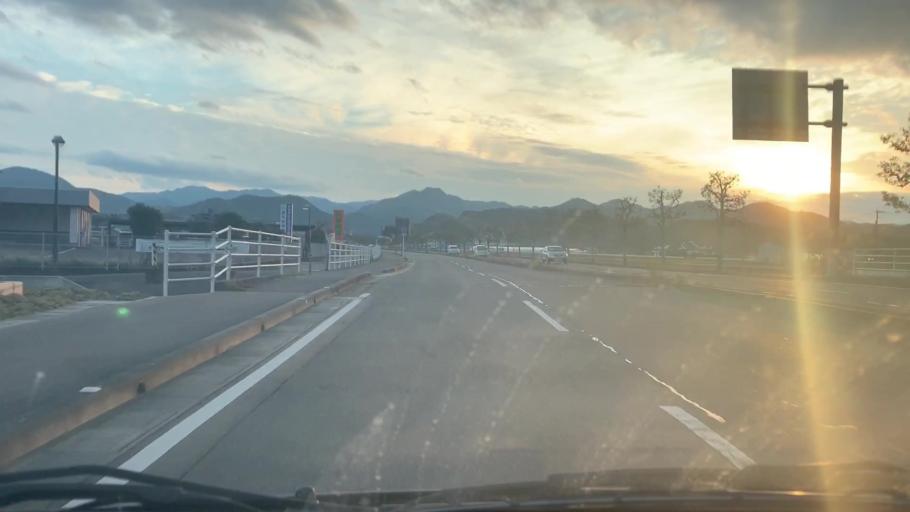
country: JP
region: Saga Prefecture
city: Kashima
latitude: 33.1184
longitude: 130.0906
